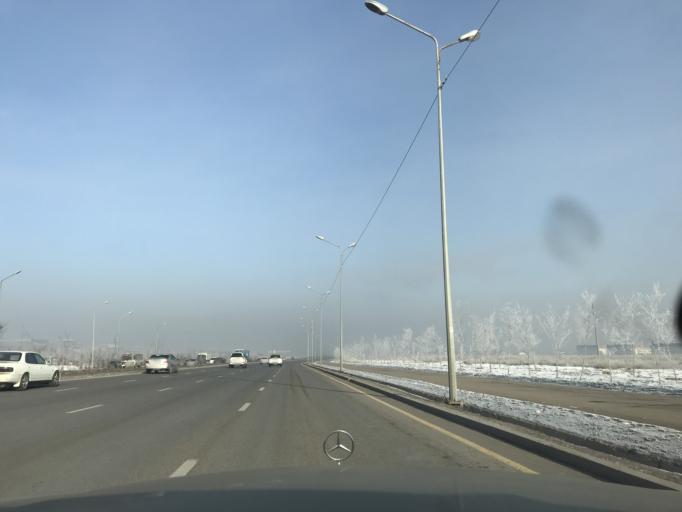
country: KZ
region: Almaty Oblysy
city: Burunday
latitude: 43.3167
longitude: 76.8340
